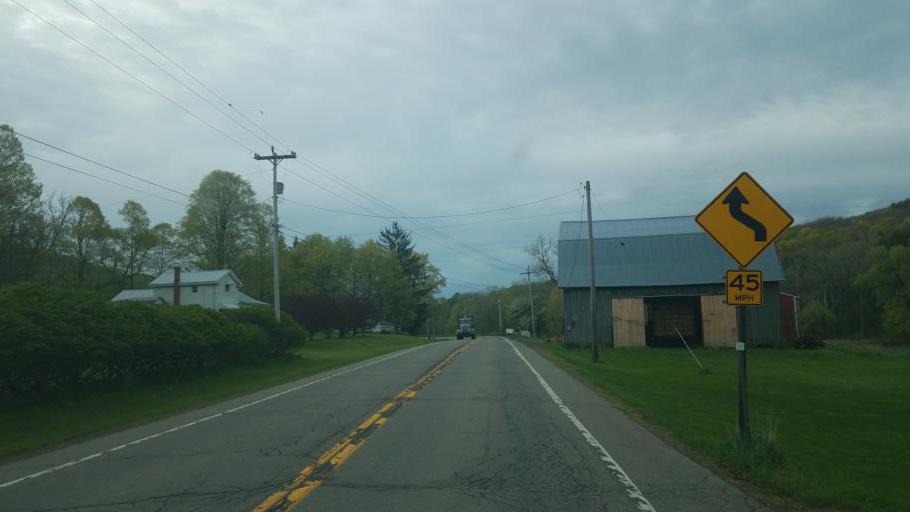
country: US
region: New York
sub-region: Steuben County
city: Canisteo
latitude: 42.2157
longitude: -77.5697
